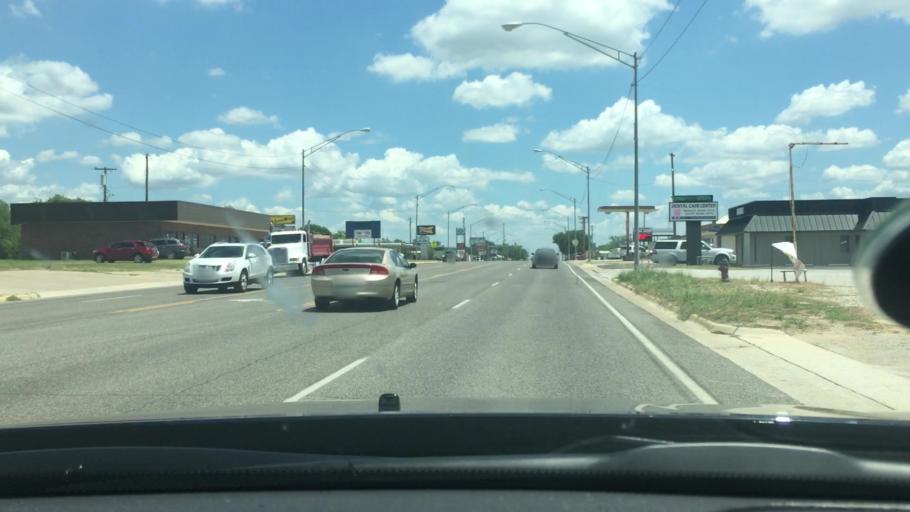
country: US
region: Oklahoma
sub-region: Carter County
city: Lone Grove
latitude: 34.1729
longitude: -97.2639
